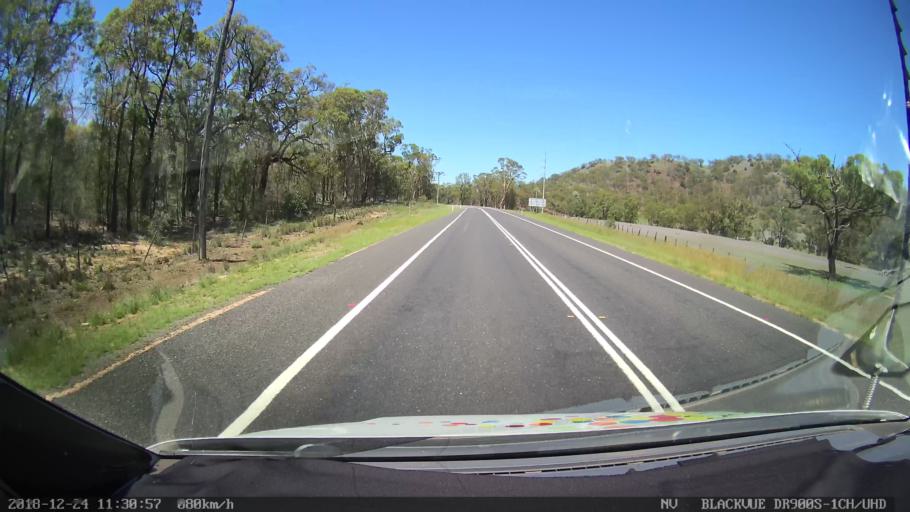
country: AU
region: New South Wales
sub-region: Upper Hunter Shire
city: Merriwa
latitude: -32.2102
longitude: 150.4623
